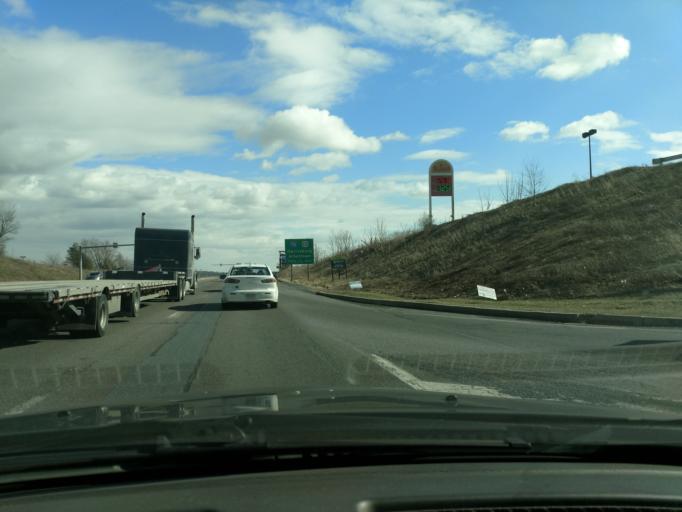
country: US
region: Pennsylvania
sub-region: Berks County
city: West Hamburg
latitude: 40.5652
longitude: -76.0076
